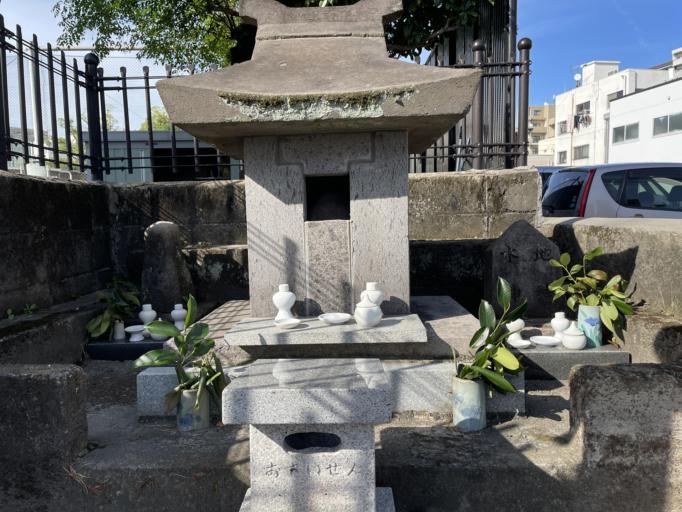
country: JP
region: Kagoshima
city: Kagoshima-shi
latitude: 31.5777
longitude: 130.5469
